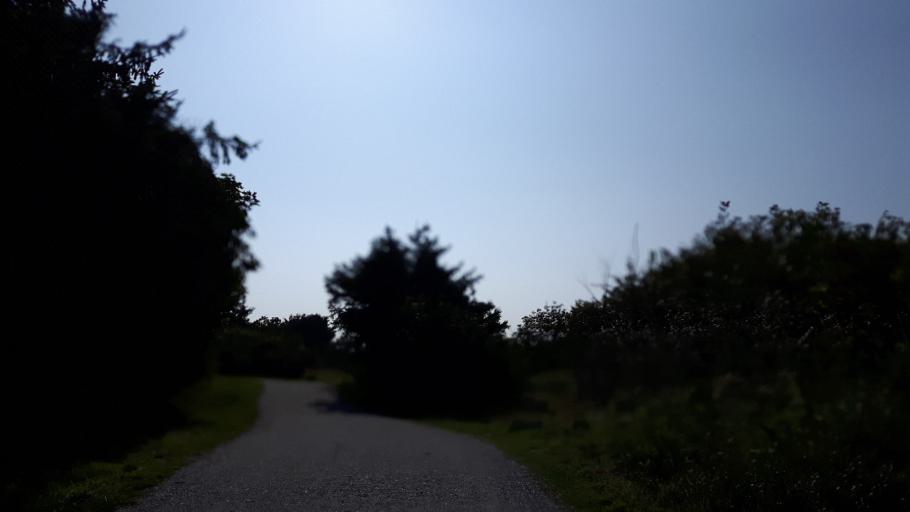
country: NL
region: Friesland
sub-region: Gemeente Ameland
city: Nes
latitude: 53.4592
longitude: 5.7885
